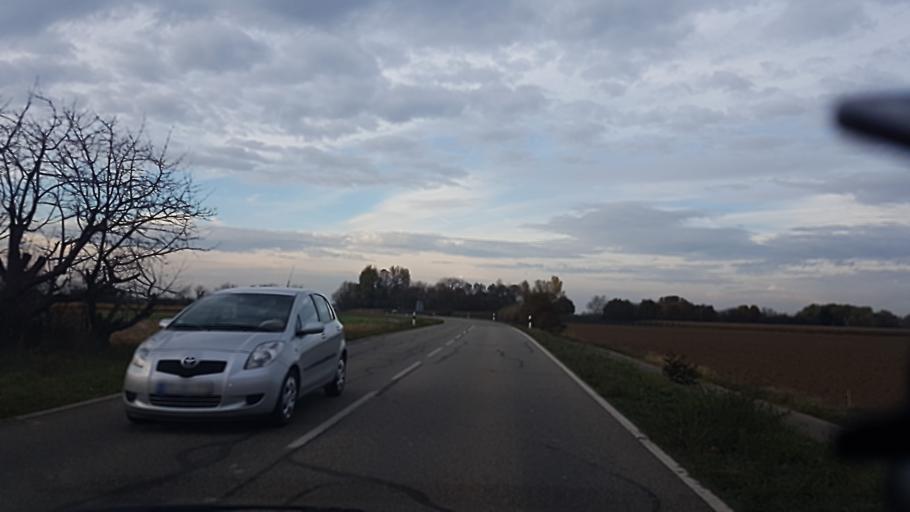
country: DE
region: Baden-Wuerttemberg
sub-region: Freiburg Region
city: Endingen
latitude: 48.1531
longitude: 7.6751
